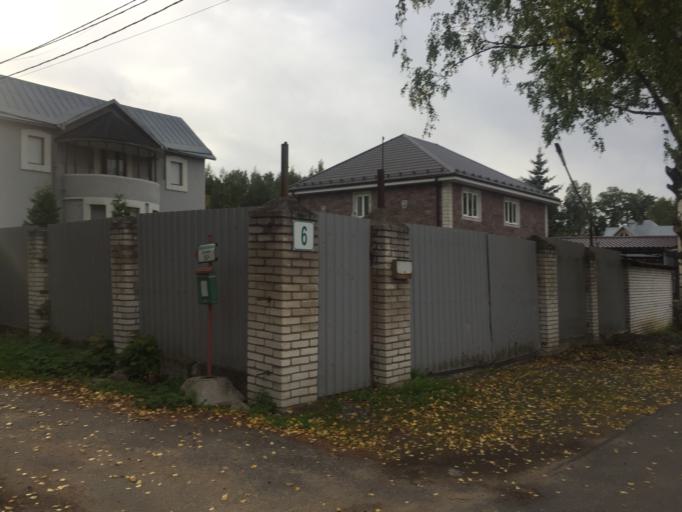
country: RU
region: Leningrad
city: Murino
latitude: 60.0480
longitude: 30.4576
